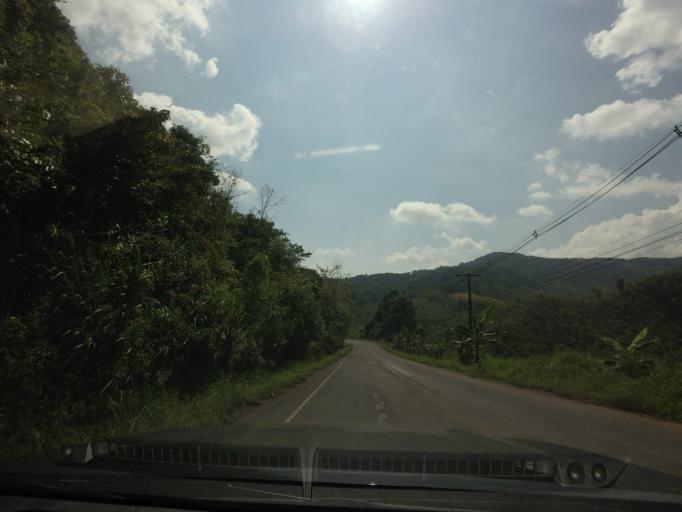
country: TH
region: Nan
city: Bo Kluea
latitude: 19.0643
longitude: 101.1002
